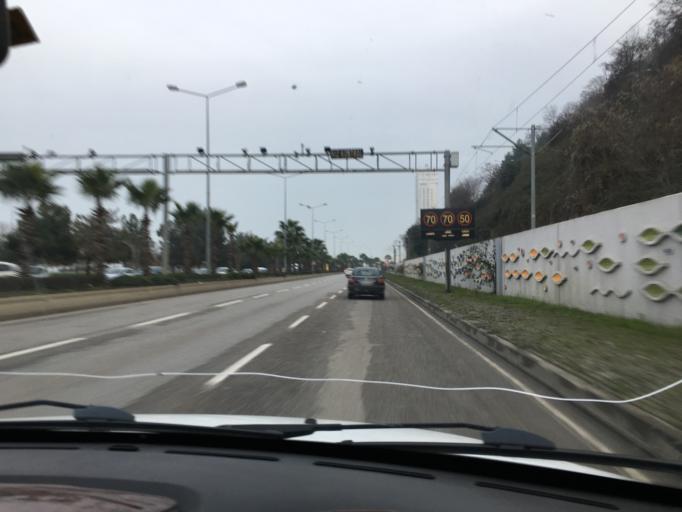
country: TR
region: Samsun
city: Samsun
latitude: 41.3177
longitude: 36.3319
